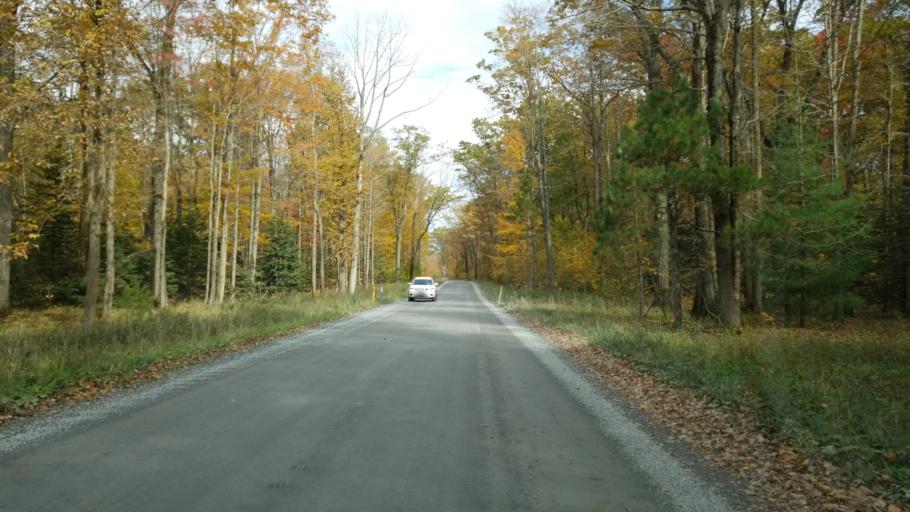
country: US
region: Pennsylvania
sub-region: Clearfield County
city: Clearfield
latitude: 41.1293
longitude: -78.5266
